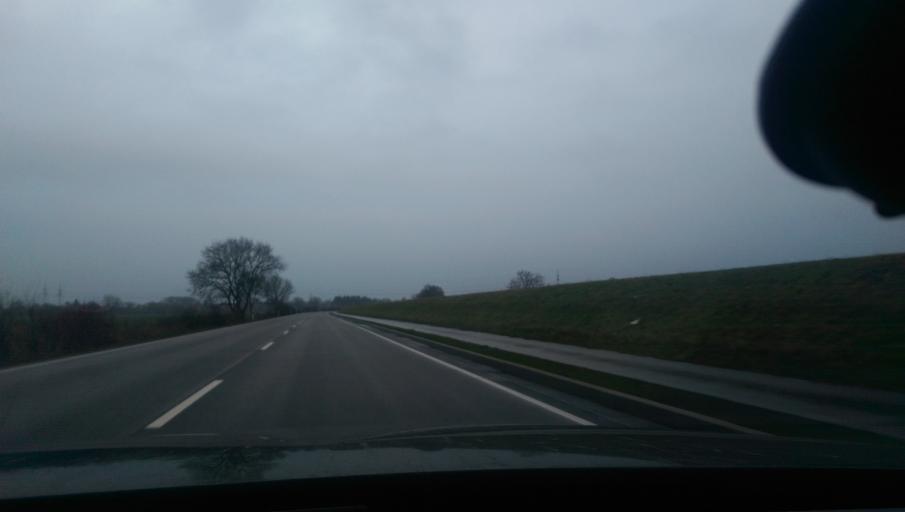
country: DE
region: Lower Saxony
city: Dorverden
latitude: 52.8663
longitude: 9.2328
